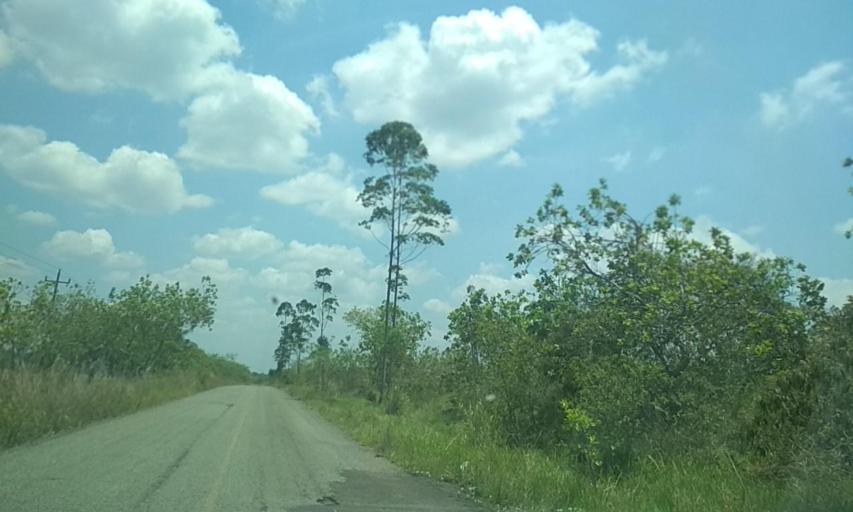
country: MX
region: Tabasco
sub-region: Huimanguillo
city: Francisco Rueda
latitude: 17.7838
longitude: -93.8289
